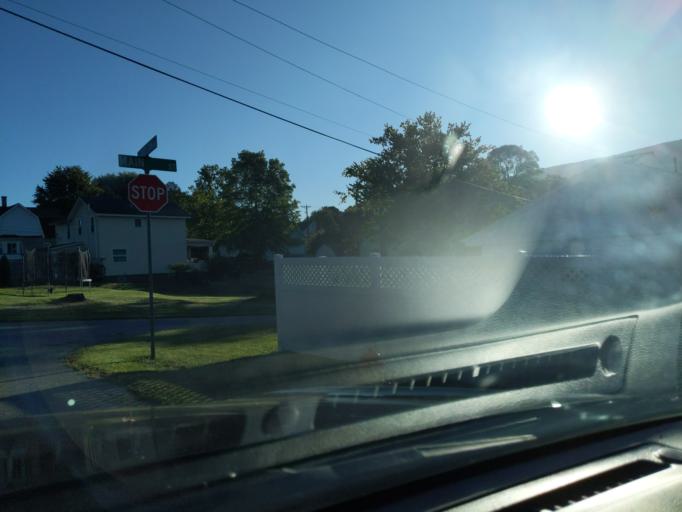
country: US
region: Pennsylvania
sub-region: Blair County
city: Greenwood
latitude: 40.5243
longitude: -78.3709
